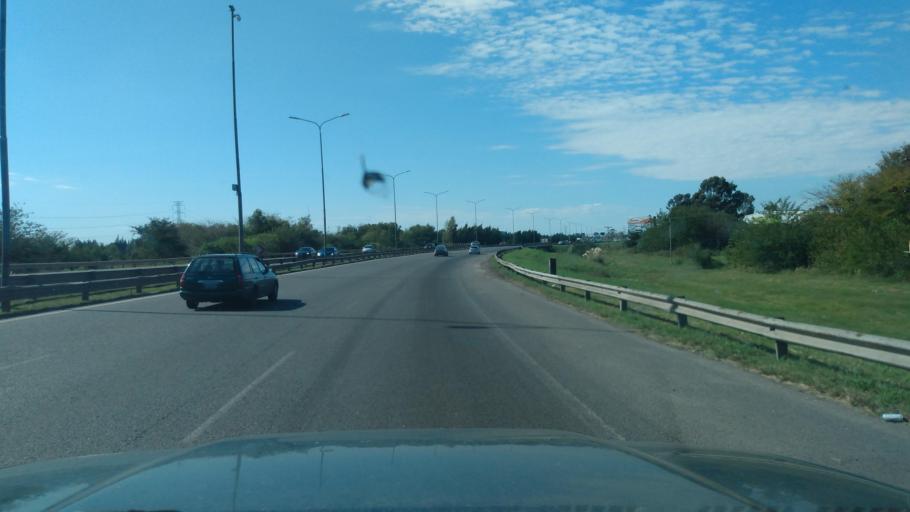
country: AR
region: Buenos Aires
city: Hurlingham
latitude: -34.5521
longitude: -58.6231
